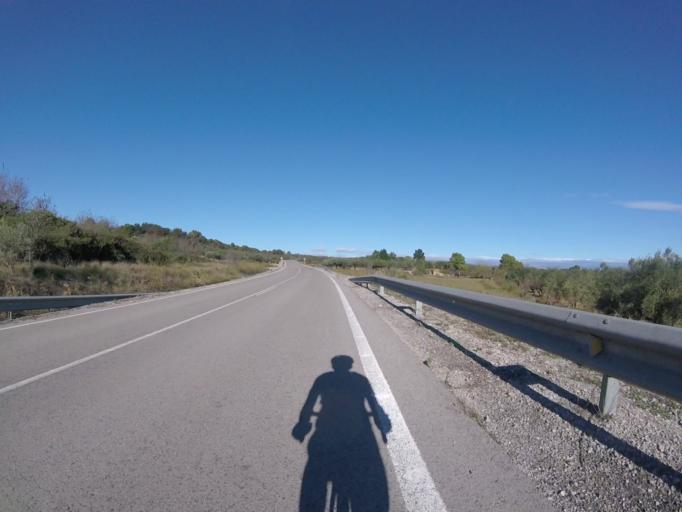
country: ES
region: Valencia
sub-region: Provincia de Castello
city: Cervera del Maestre
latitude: 40.4690
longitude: 0.2458
